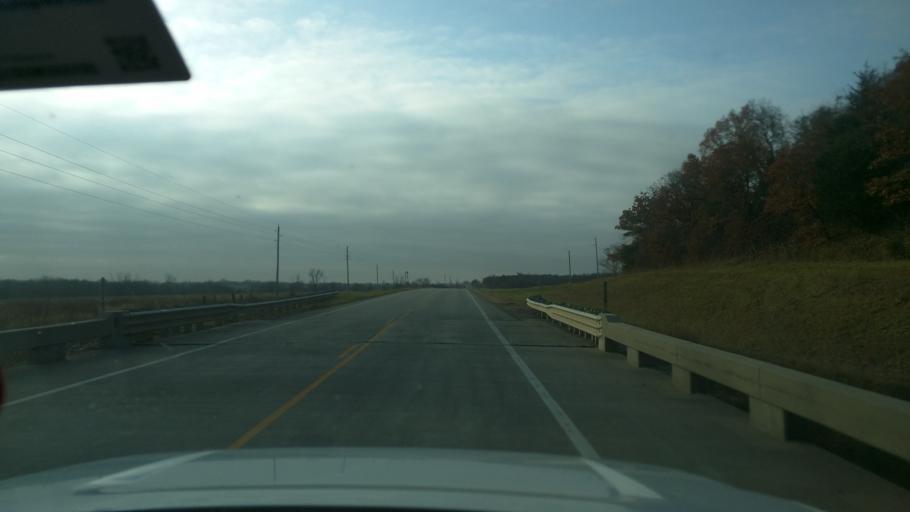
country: US
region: Kansas
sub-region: Greenwood County
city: Eureka
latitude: 37.7390
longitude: -96.2296
